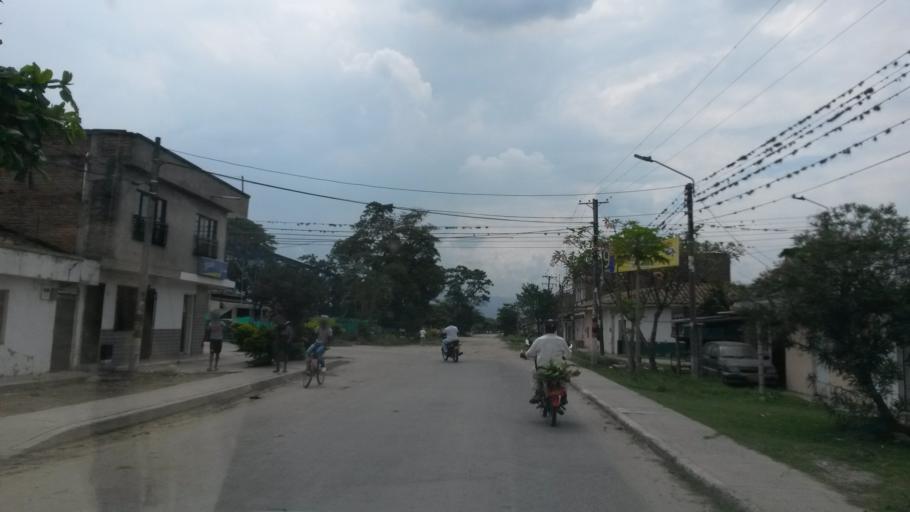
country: CO
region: Cauca
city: Padilla
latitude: 3.2263
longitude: -76.3146
